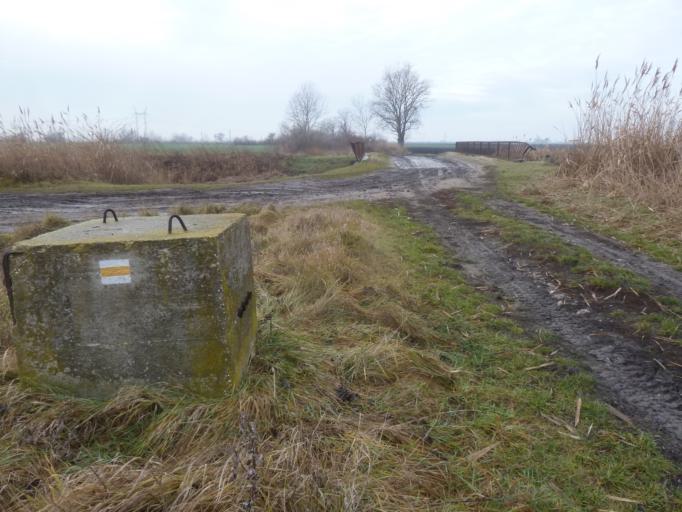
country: HU
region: Bacs-Kiskun
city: Szabadszallas
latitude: 46.9181
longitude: 19.2342
